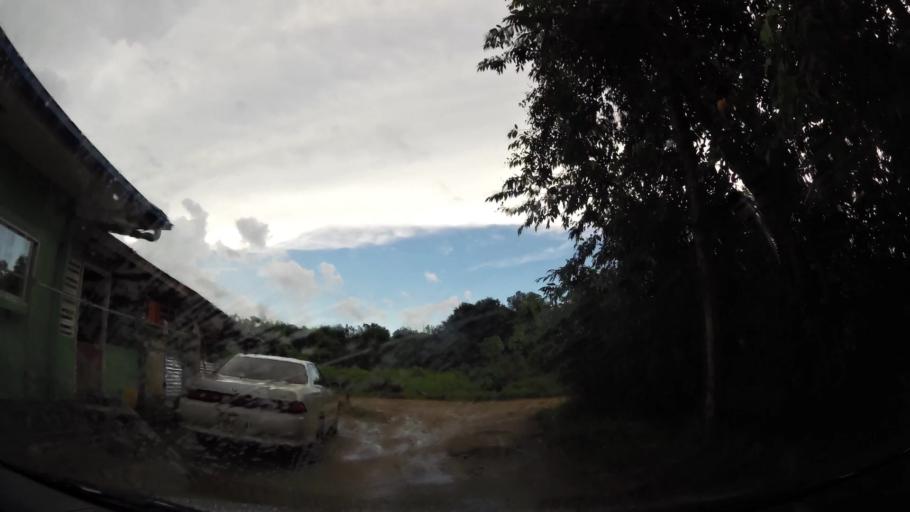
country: SR
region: Commewijne
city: Nieuw Amsterdam
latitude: 5.8870
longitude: -55.0572
